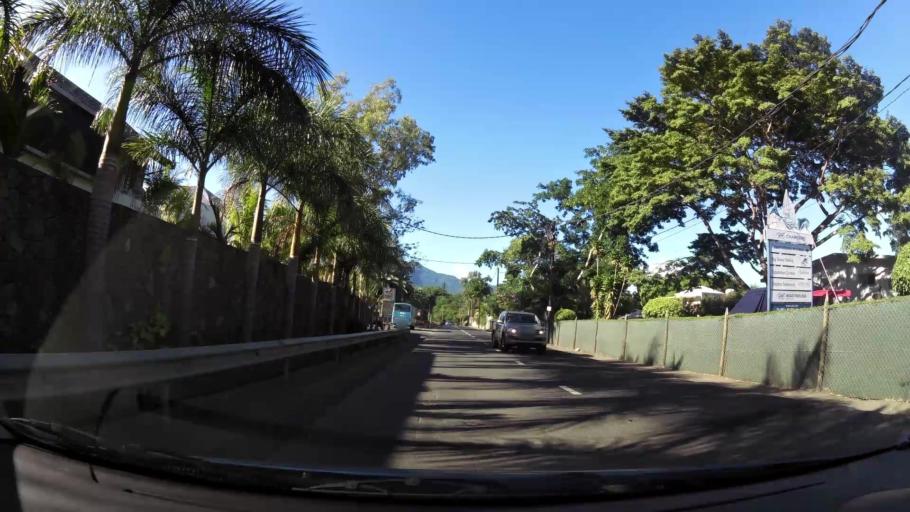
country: MU
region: Black River
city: Grande Riviere Noire
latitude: -20.3569
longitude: 57.3673
